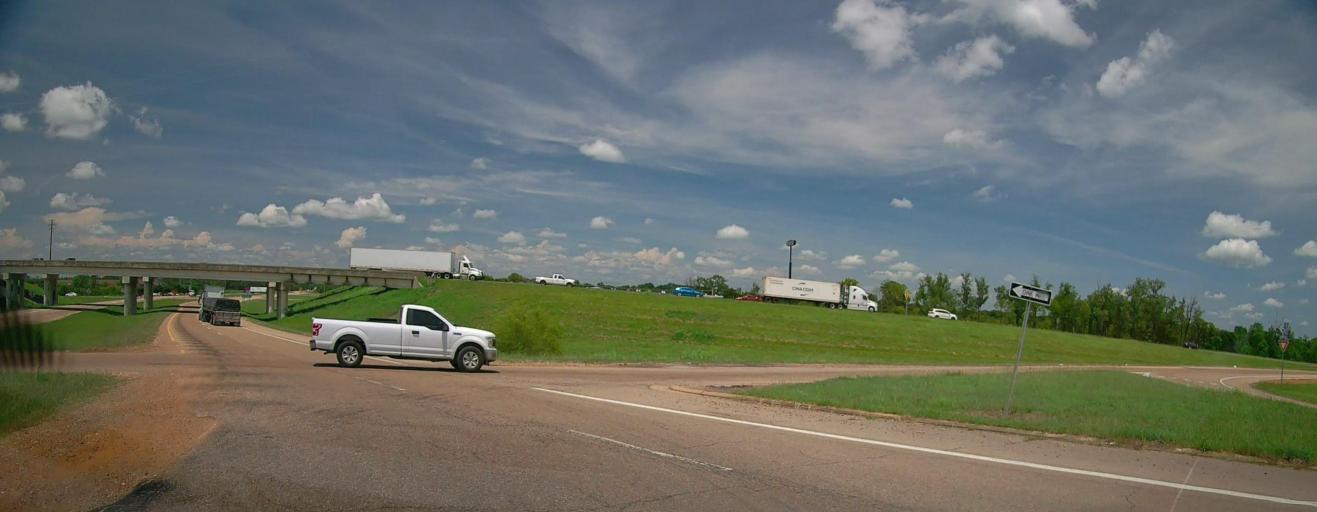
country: US
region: Mississippi
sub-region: Lee County
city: Tupelo
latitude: 34.3126
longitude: -88.7883
